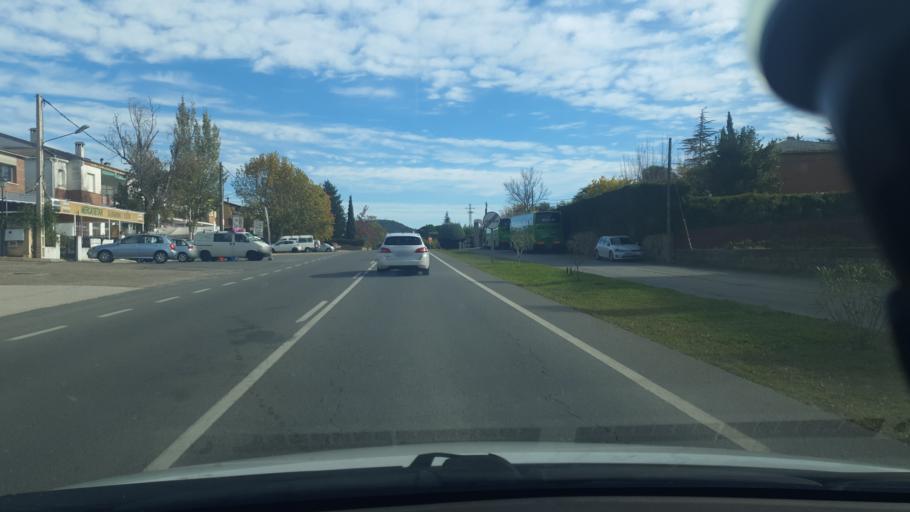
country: ES
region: Castille and Leon
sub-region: Provincia de Avila
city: La Adrada
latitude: 40.3063
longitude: -4.6477
